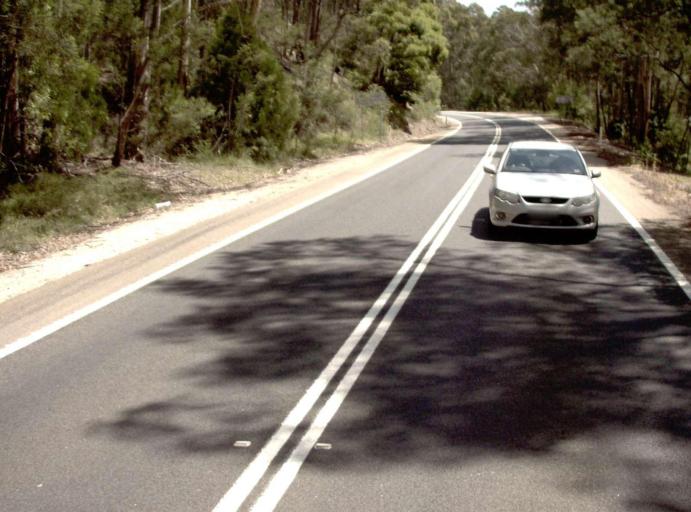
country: AU
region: New South Wales
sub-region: Bombala
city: Bombala
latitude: -37.5638
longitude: 149.3460
